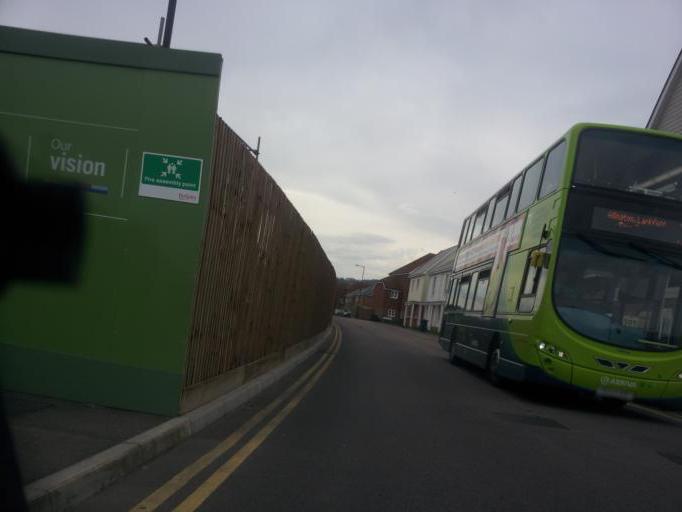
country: GB
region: England
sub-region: Kent
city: Snodland
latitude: 51.3362
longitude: 0.4398
